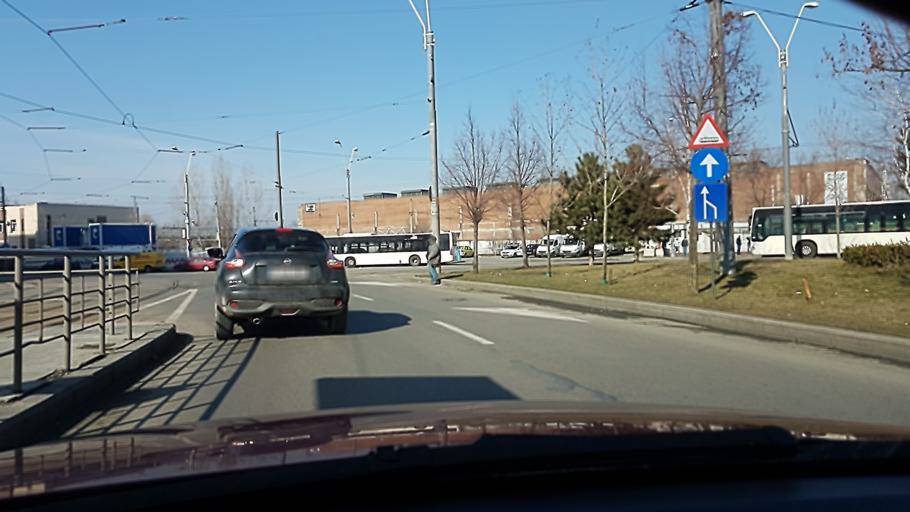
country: RO
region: Ilfov
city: Dobroesti
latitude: 44.4268
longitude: 26.1791
